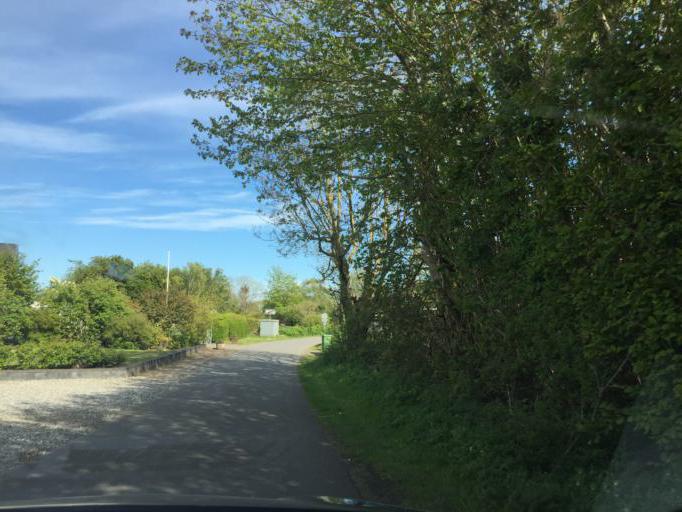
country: DK
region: South Denmark
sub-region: Fredericia Kommune
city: Taulov
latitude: 55.5263
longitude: 9.5524
